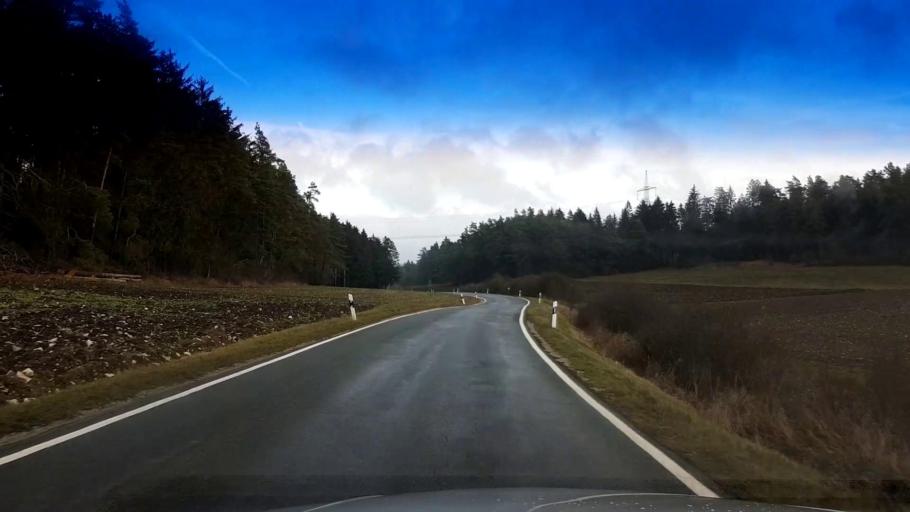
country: DE
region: Bavaria
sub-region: Upper Franconia
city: Poxdorf
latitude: 49.9241
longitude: 11.1034
